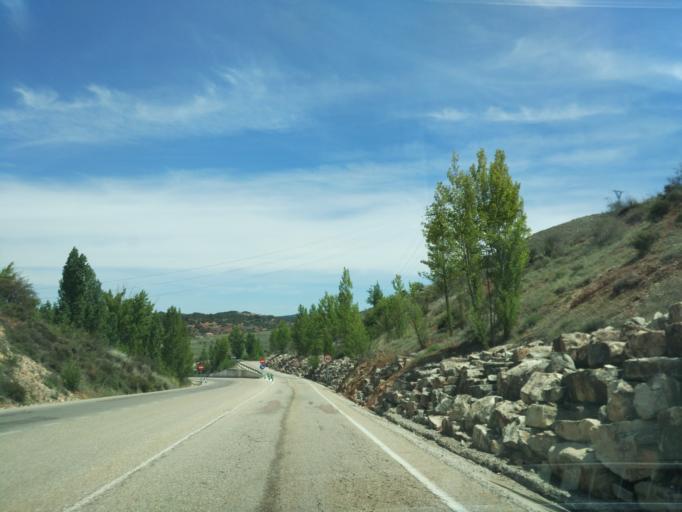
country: ES
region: Castille-La Mancha
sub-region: Provincia de Guadalajara
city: Siguenza
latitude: 41.0572
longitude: -2.6497
